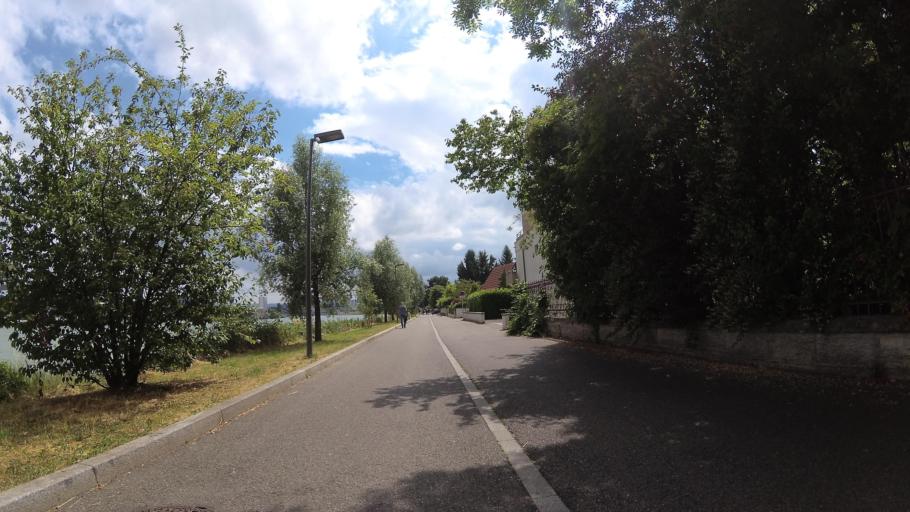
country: FR
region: Alsace
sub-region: Departement du Haut-Rhin
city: Village-Neuf
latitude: 47.5867
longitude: 7.5855
